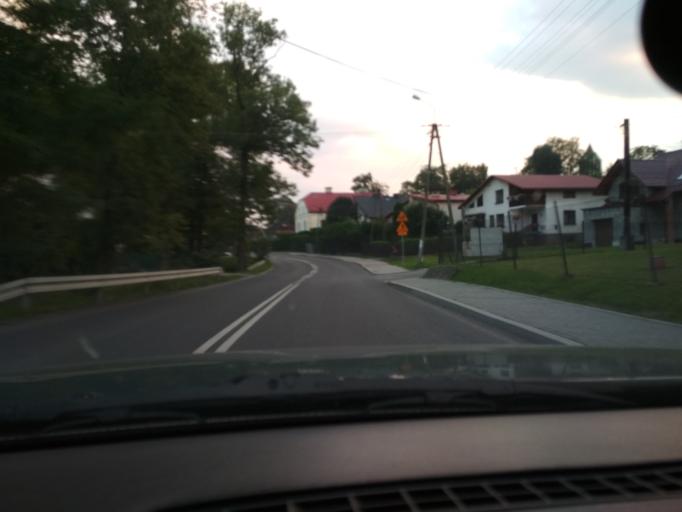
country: PL
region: Silesian Voivodeship
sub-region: Powiat bielski
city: Mazancowice
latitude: 49.8448
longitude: 18.9421
